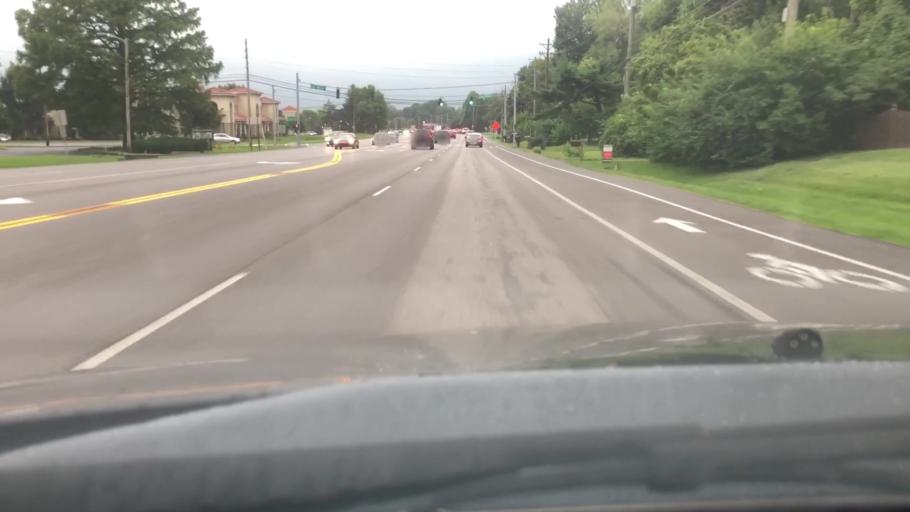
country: US
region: Kentucky
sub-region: Jefferson County
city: Hurstbourne Acres
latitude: 38.2106
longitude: -85.5860
